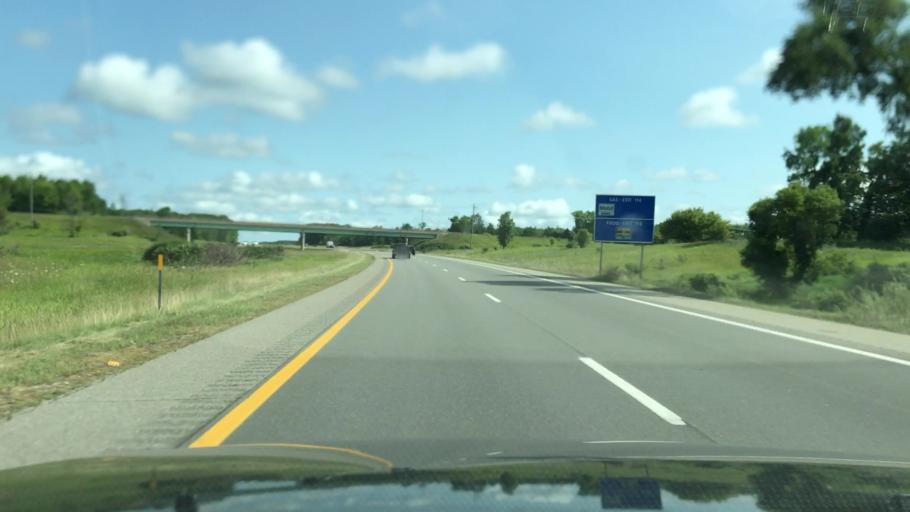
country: US
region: Michigan
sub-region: Montcalm County
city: Howard City
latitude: 43.3208
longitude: -85.5160
